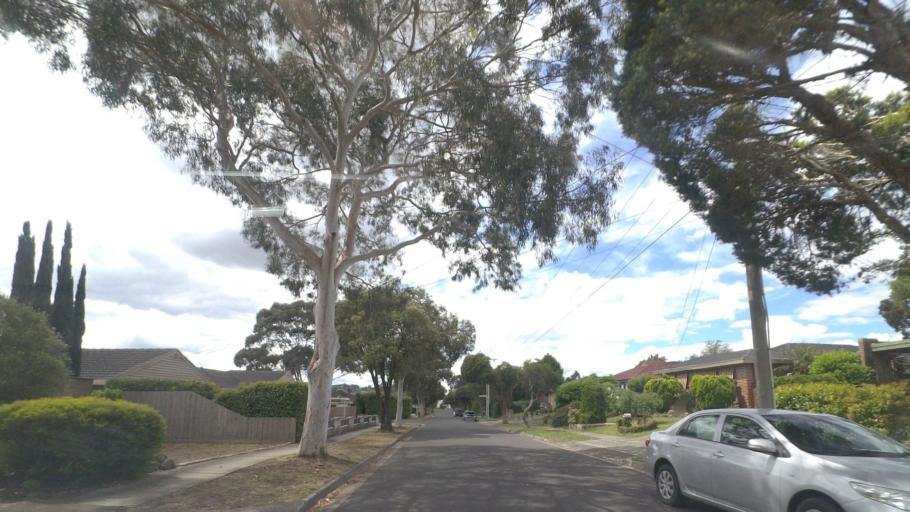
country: AU
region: Victoria
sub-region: Maroondah
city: Heathmont
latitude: -37.8458
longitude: 145.2455
